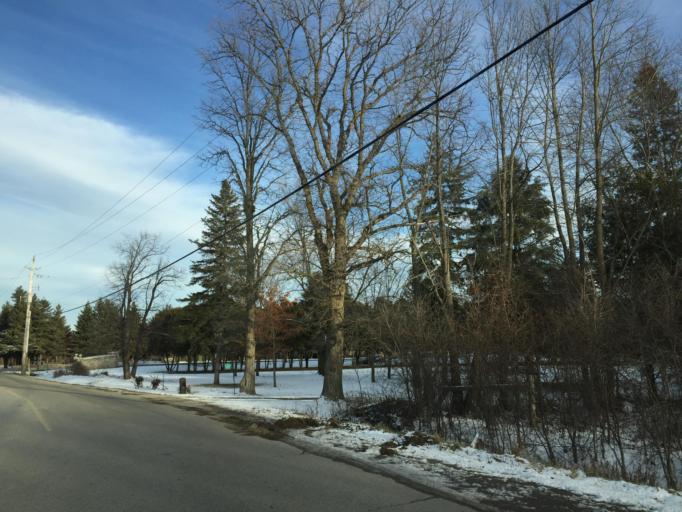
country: CA
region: Ontario
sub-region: Wellington County
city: Guelph
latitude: 43.4997
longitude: -80.2608
